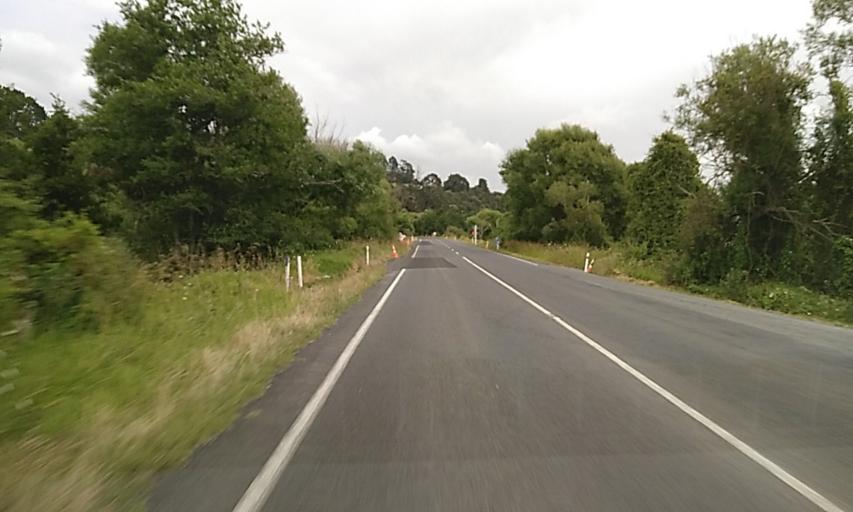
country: NZ
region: Auckland
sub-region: Auckland
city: Pukekohe East
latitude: -37.3033
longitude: 174.9496
